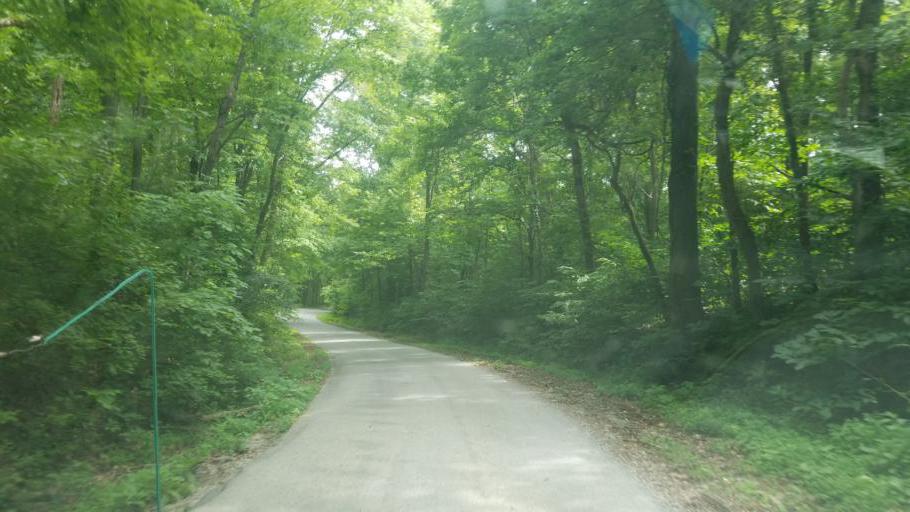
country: US
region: Illinois
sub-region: Jackson County
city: Murphysboro
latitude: 37.6227
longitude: -89.3688
